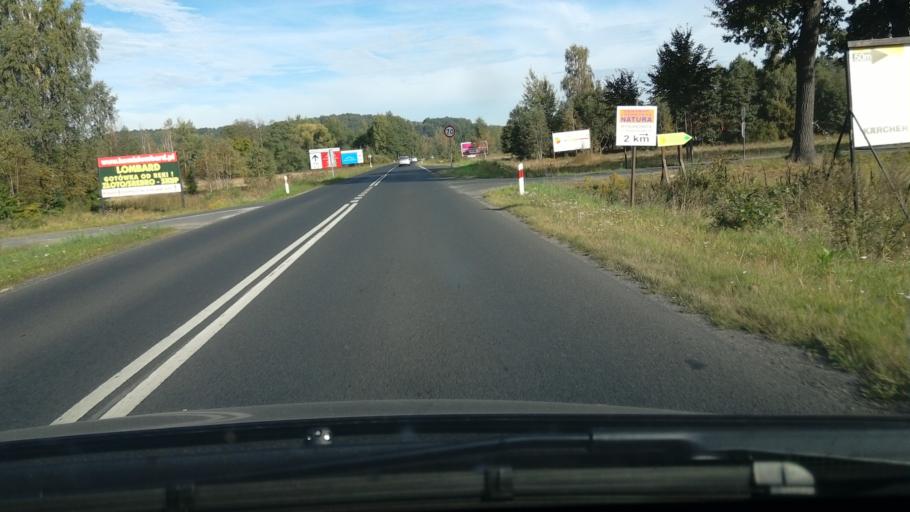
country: PL
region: Lower Silesian Voivodeship
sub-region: Powiat jeleniogorski
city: Myslakowice
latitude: 50.8319
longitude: 15.7748
